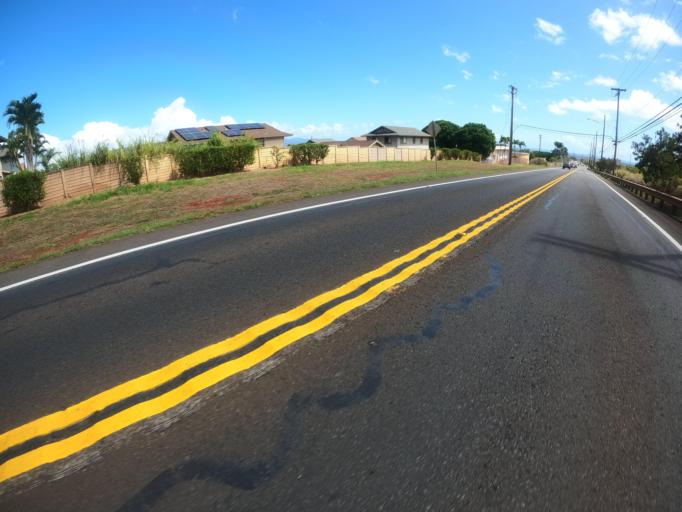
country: US
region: Hawaii
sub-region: Honolulu County
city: Village Park
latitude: 21.4000
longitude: -158.0396
